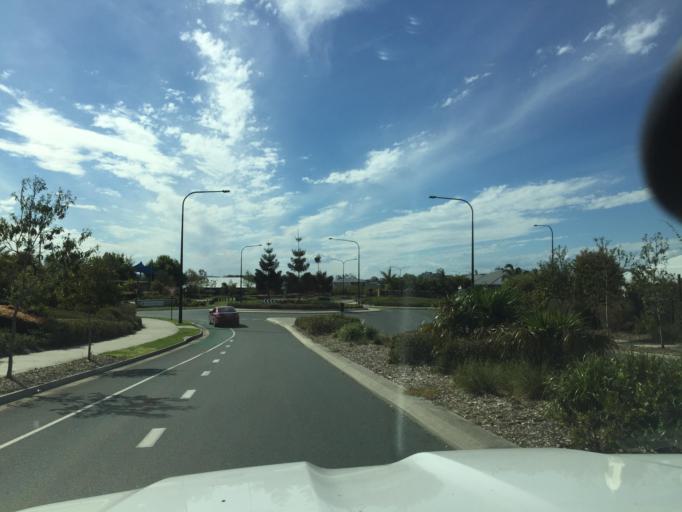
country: AU
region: Queensland
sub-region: Moreton Bay
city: Morayfield
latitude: -27.1207
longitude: 152.9952
